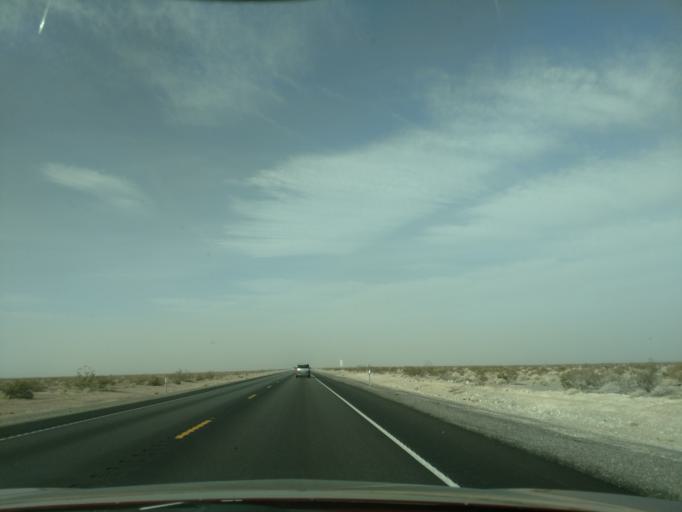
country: US
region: Nevada
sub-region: Nye County
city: Beatty
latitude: 36.6336
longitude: -116.3588
